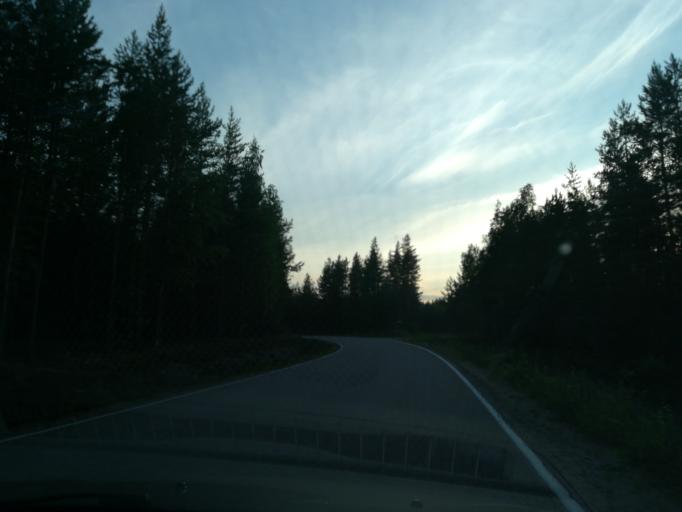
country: FI
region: South Karelia
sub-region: Lappeenranta
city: Joutseno
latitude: 61.3462
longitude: 28.4241
